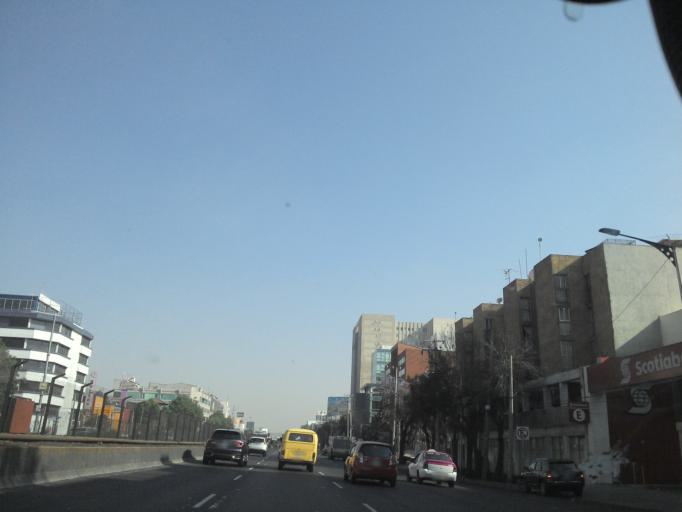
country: MX
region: Mexico City
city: Colonia Nativitas
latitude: 19.3962
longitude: -99.1376
